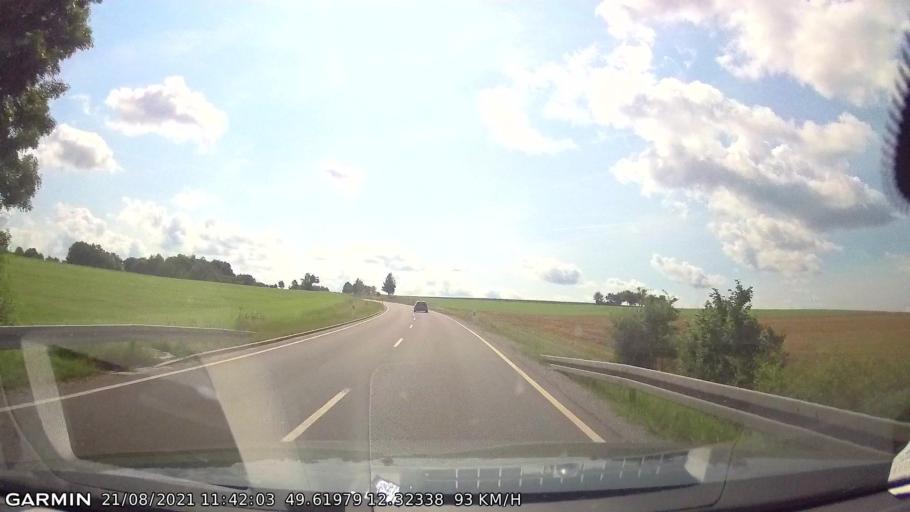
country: DE
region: Bavaria
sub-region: Upper Palatinate
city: Vohenstrauss
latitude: 49.6197
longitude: 12.3233
